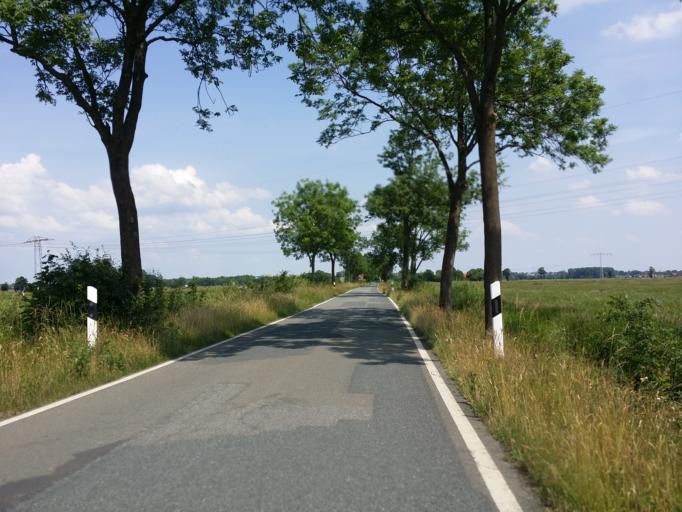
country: DE
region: Lower Saxony
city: Lemwerder
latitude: 53.1452
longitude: 8.5781
